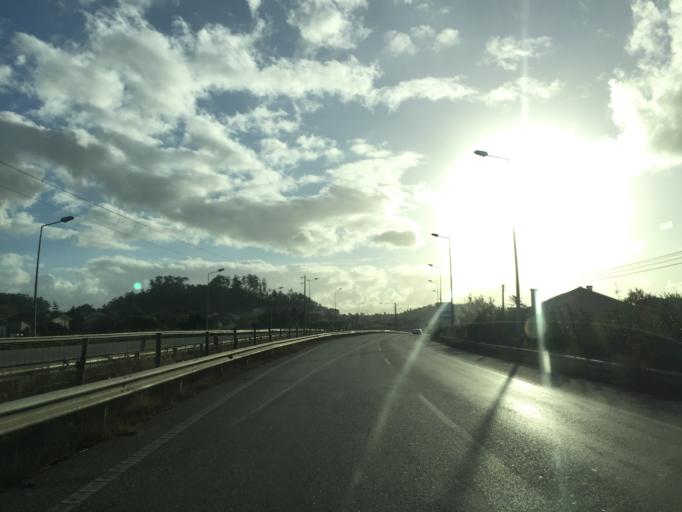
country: PT
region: Coimbra
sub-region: Coimbra
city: Coimbra
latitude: 40.2031
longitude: -8.4788
